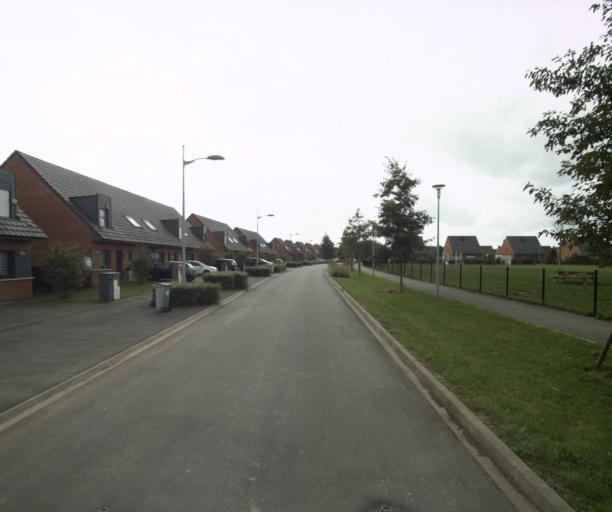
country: FR
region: Nord-Pas-de-Calais
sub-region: Departement du Nord
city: Saint-Andre-lez-Lille
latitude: 50.6716
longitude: 3.0447
